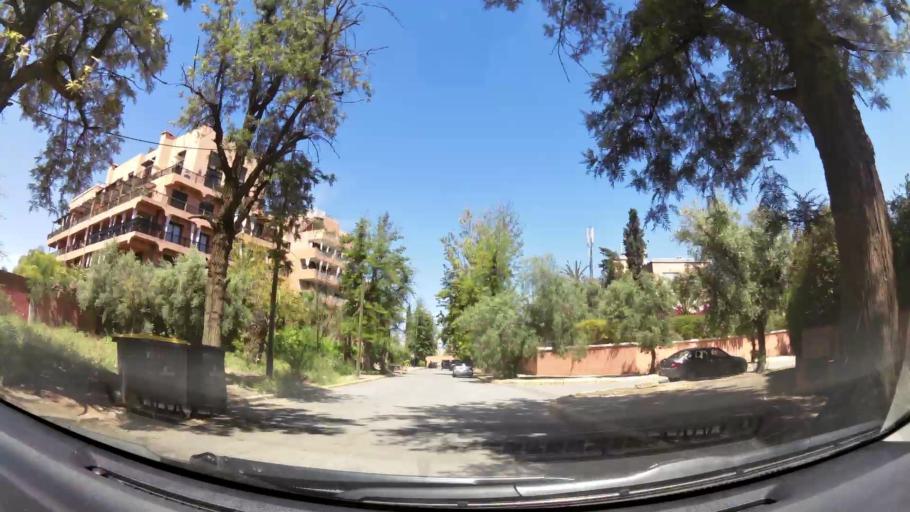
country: MA
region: Marrakech-Tensift-Al Haouz
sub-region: Marrakech
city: Marrakesh
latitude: 31.6251
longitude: -8.0059
